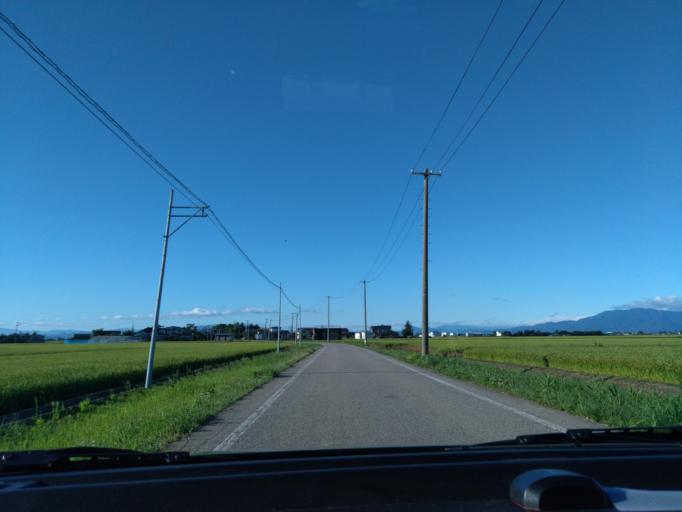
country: JP
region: Akita
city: Omagari
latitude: 39.4144
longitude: 140.5146
